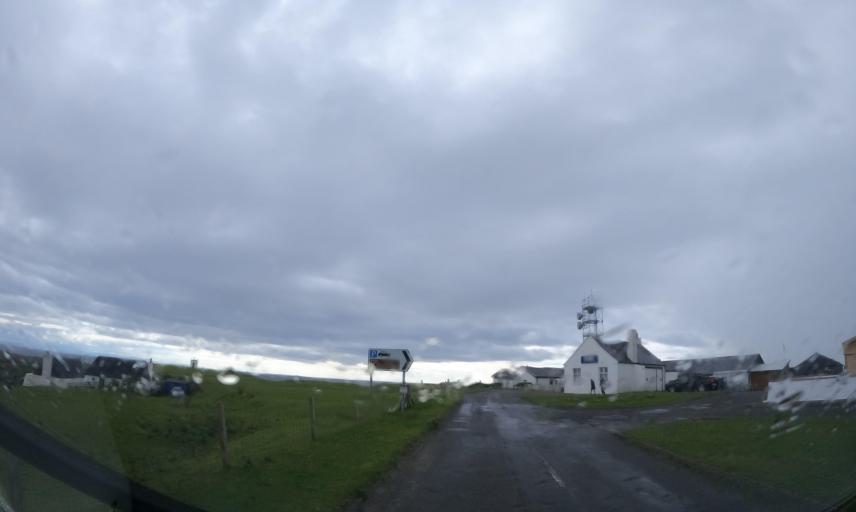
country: GB
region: Scotland
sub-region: Eilean Siar
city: Barra
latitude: 56.5010
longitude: -6.8074
